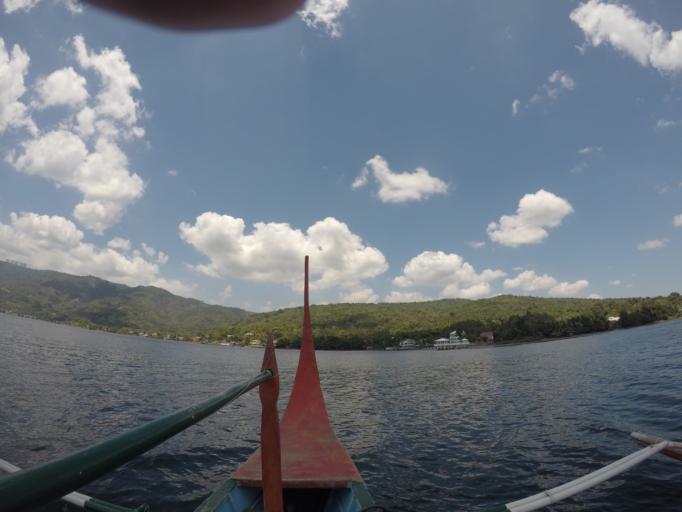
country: PH
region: Calabarzon
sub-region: Province of Batangas
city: Sampaloc
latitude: 14.0804
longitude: 120.9888
